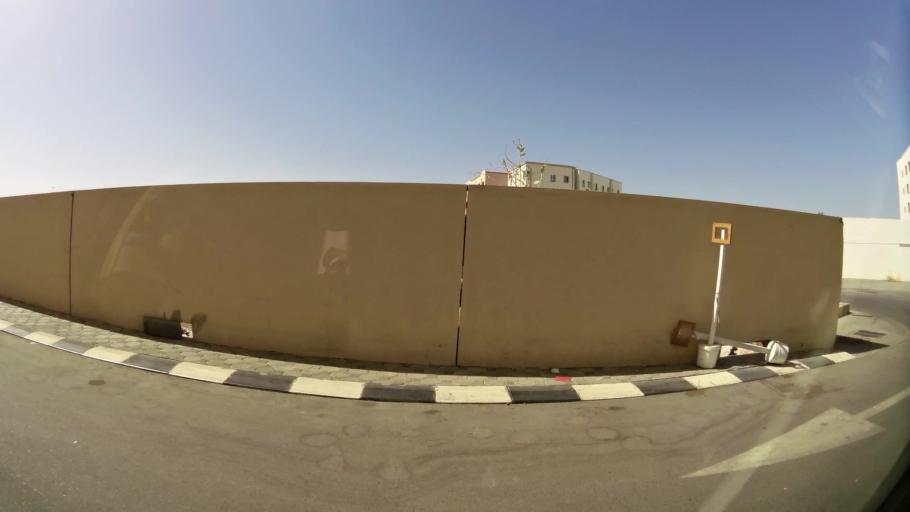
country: OM
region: Muhafazat Masqat
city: As Sib al Jadidah
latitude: 23.6110
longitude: 58.2436
